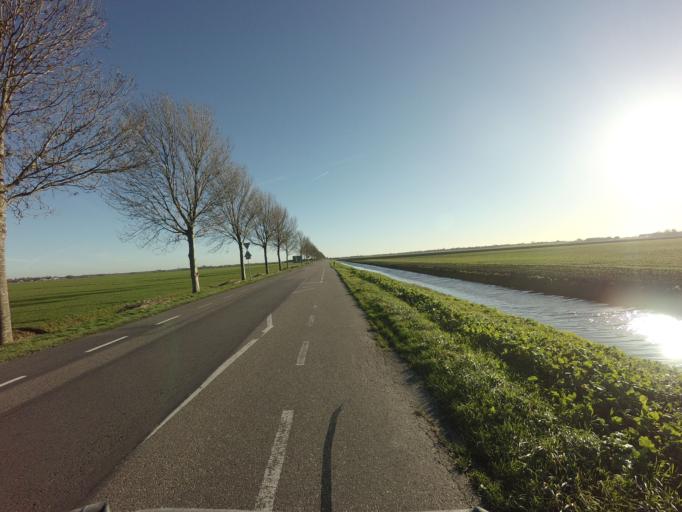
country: NL
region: South Holland
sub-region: Gemeente Nieuwkoop
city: Nieuwkoop
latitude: 52.2005
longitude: 4.7841
